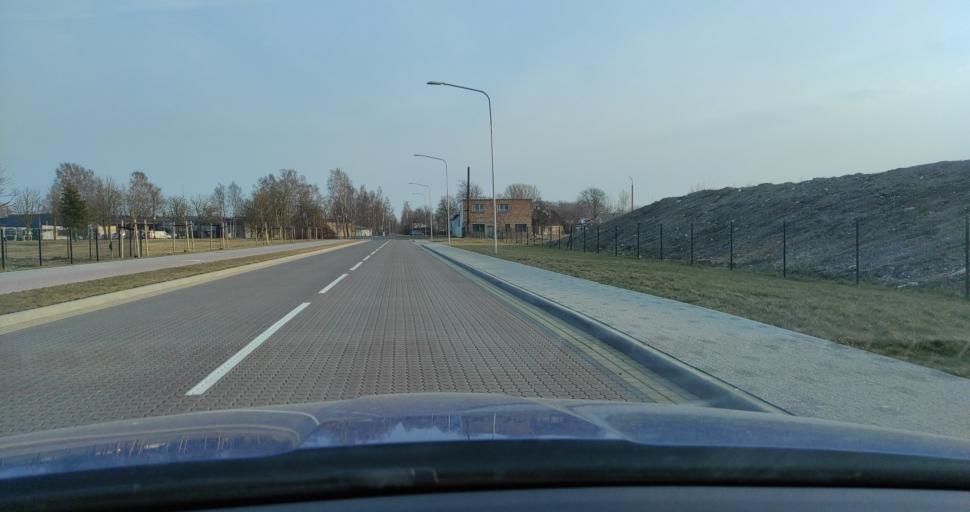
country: LV
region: Ventspils
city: Ventspils
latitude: 57.3847
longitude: 21.5818
